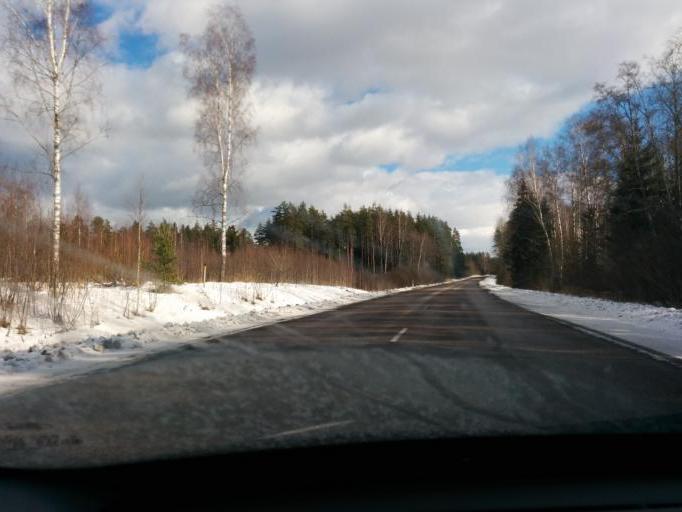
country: LV
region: Gulbenes Rajons
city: Gulbene
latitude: 57.2295
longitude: 26.5280
